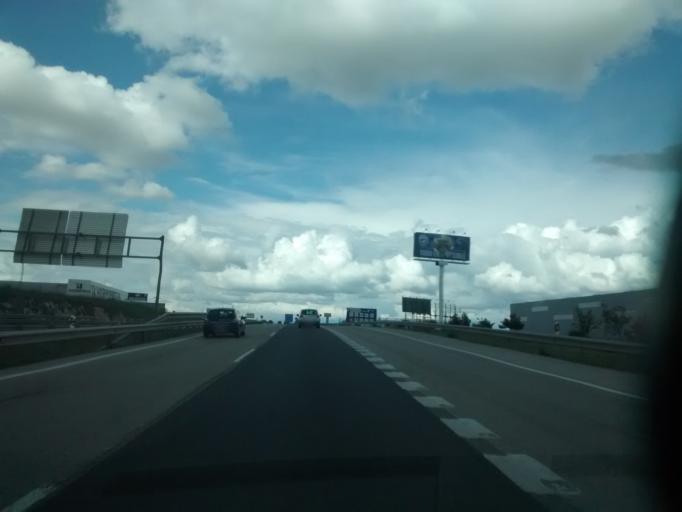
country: ES
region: Castille-La Mancha
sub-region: Provincia de Guadalajara
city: Torija
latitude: 40.7495
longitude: -3.0271
